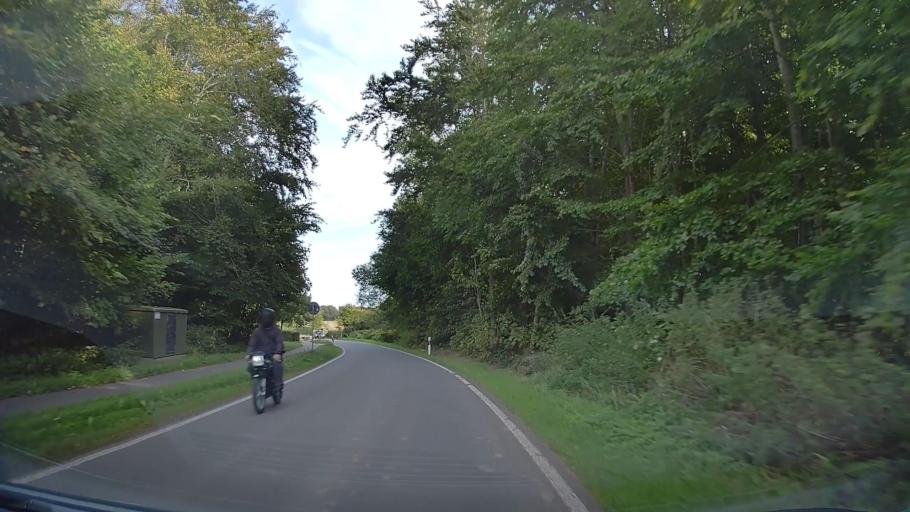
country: DE
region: Schleswig-Holstein
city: Dollerup
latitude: 54.8044
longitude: 9.7071
